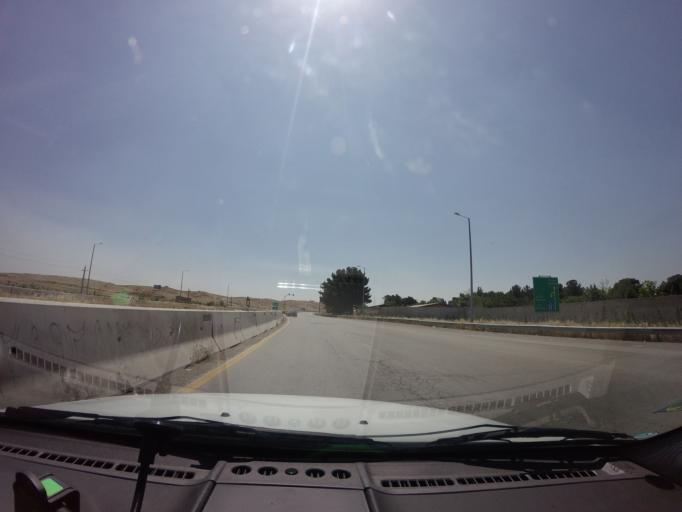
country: IR
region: Tehran
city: Eslamshahr
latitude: 35.4372
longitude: 51.2068
